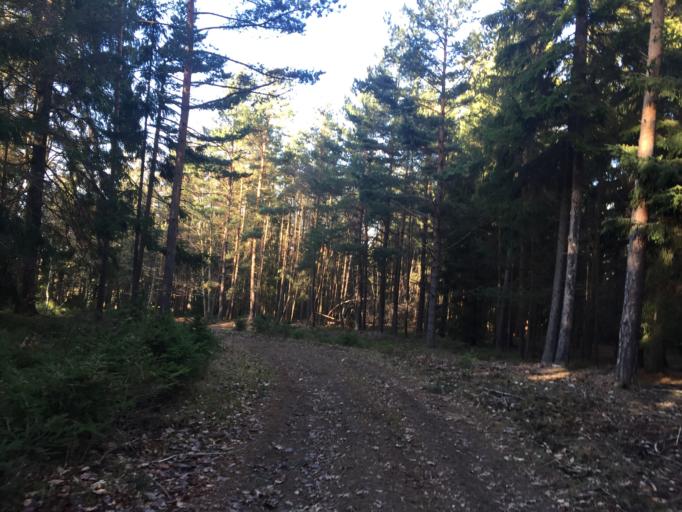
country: DE
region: Thuringia
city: Bad Blankenburg
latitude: 50.6638
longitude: 11.2683
